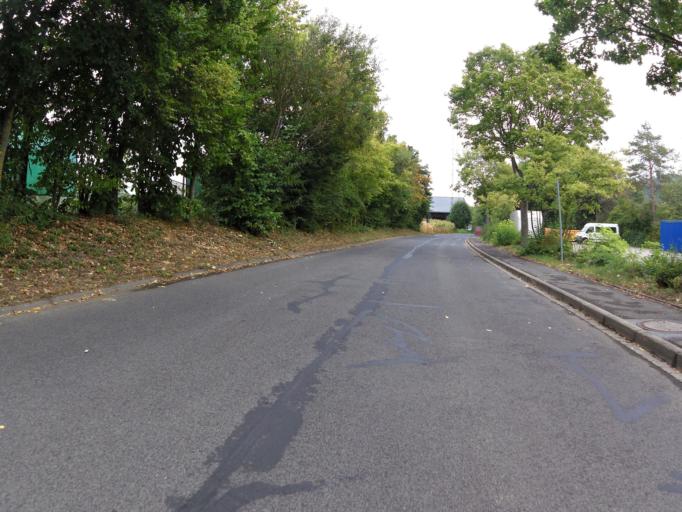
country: DE
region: Bavaria
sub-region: Regierungsbezirk Unterfranken
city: Guntersleben
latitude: 49.8750
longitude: 9.9084
